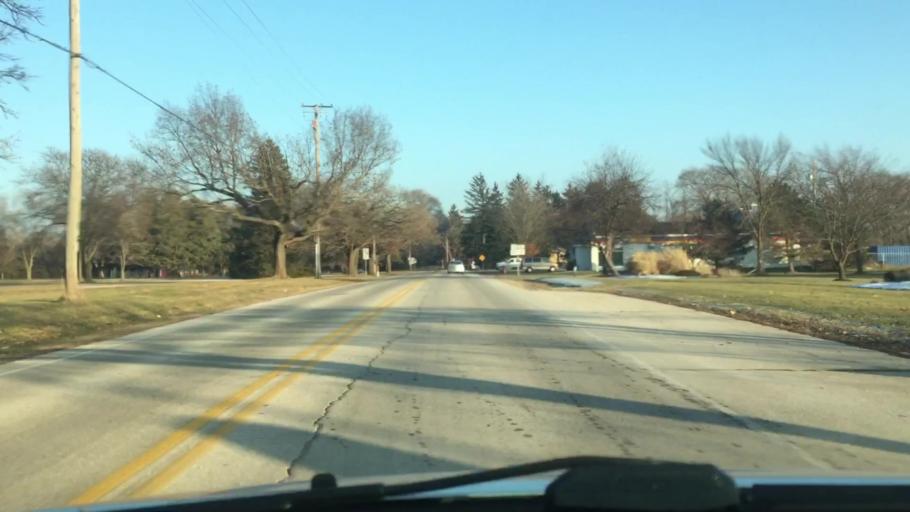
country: US
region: Wisconsin
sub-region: Waukesha County
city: Dousman
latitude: 43.0104
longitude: -88.4650
